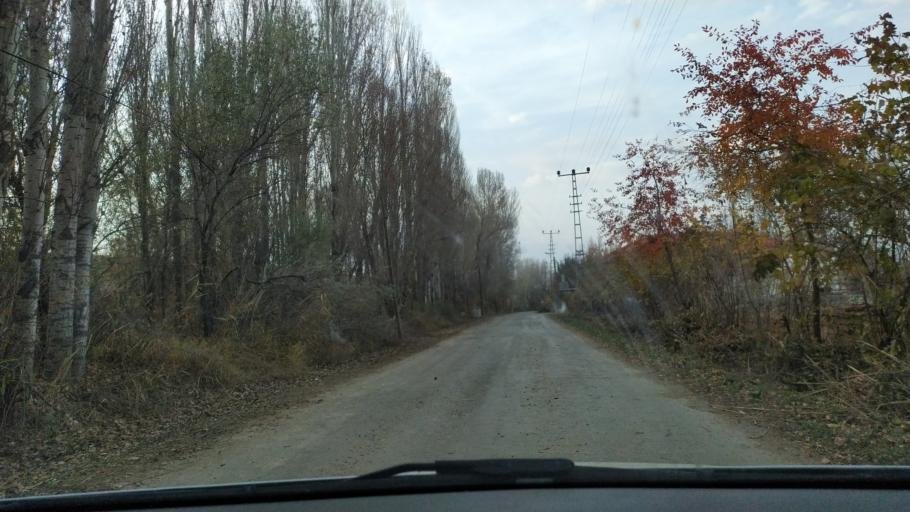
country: TR
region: Kayseri
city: Akkisla
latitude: 38.9972
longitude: 36.1143
